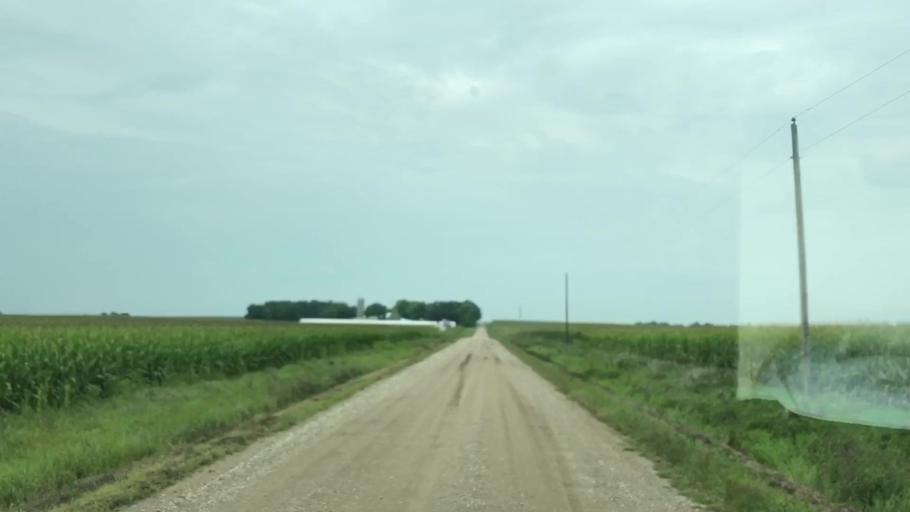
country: US
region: Iowa
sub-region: O'Brien County
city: Sheldon
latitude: 43.1865
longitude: -95.9017
